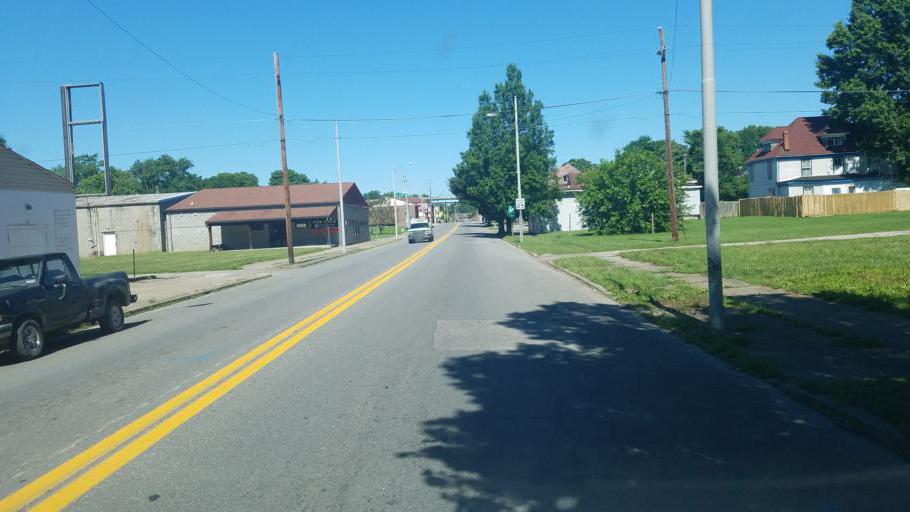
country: US
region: West Virginia
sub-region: Cabell County
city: Huntington
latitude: 38.4295
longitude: -82.3861
